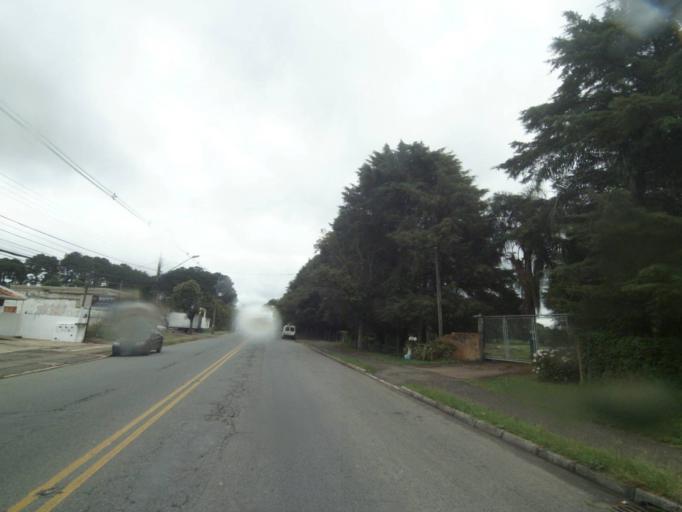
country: BR
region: Parana
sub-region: Curitiba
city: Curitiba
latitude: -25.4480
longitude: -49.3502
